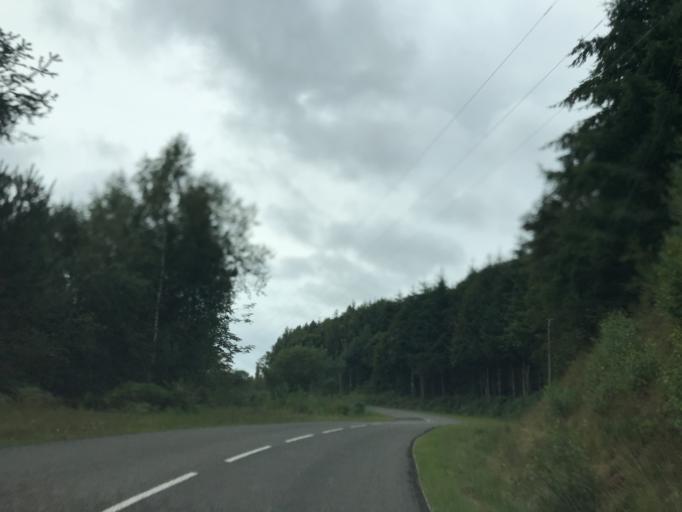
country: FR
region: Rhone-Alpes
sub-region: Departement de la Loire
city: Sail-sous-Couzan
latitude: 45.6945
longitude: 3.8714
